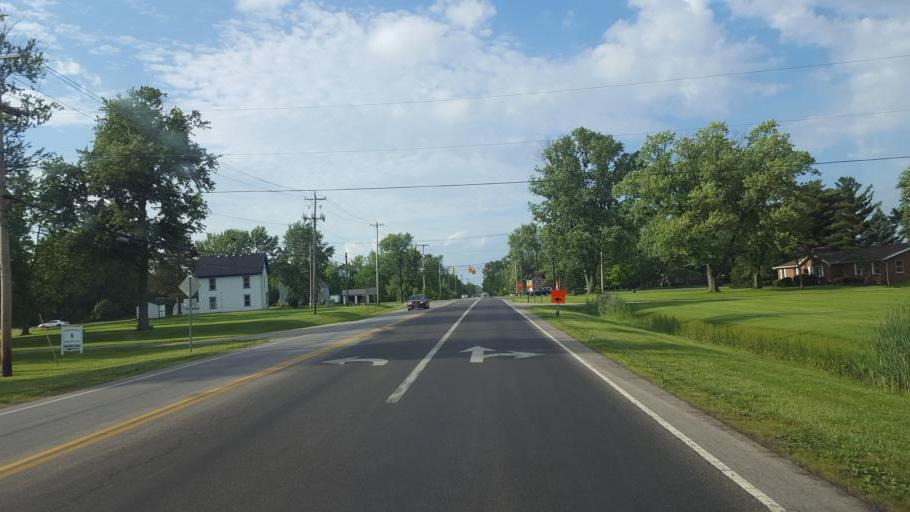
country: US
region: Ohio
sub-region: Delaware County
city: Lewis Center
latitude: 40.1972
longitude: -82.9903
